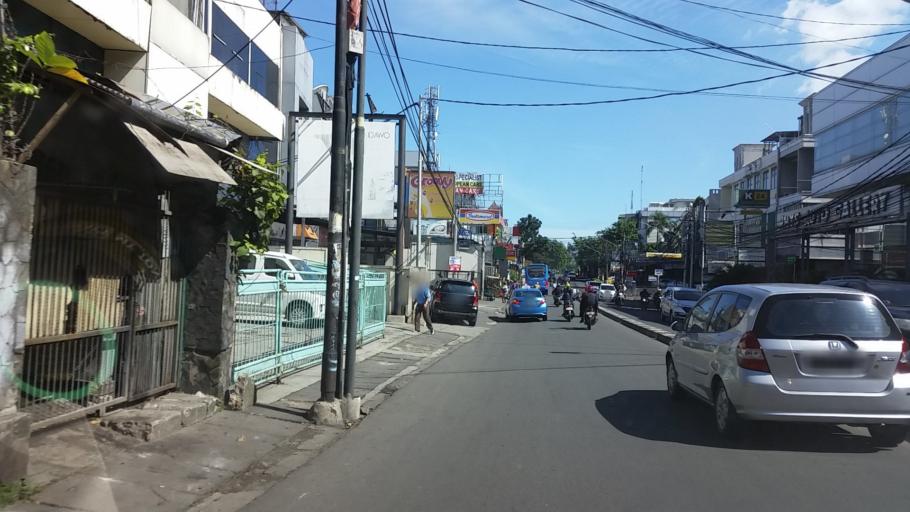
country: ID
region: Jakarta Raya
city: Jakarta
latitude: -6.2616
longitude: 106.7887
